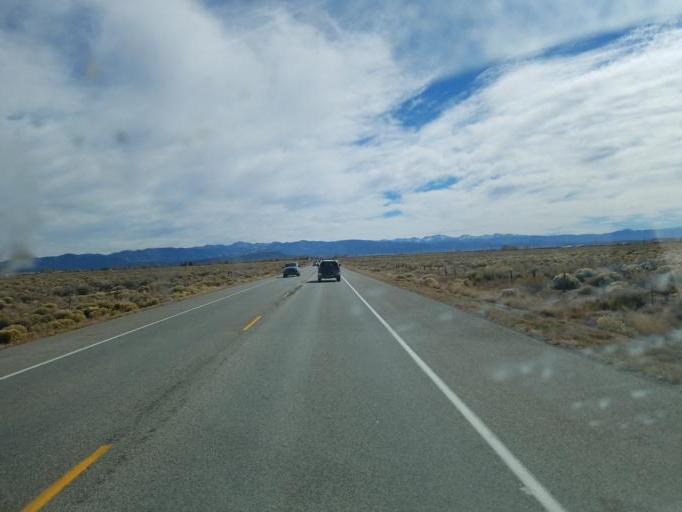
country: US
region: Colorado
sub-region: Costilla County
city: San Luis
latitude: 37.4449
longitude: -105.5340
